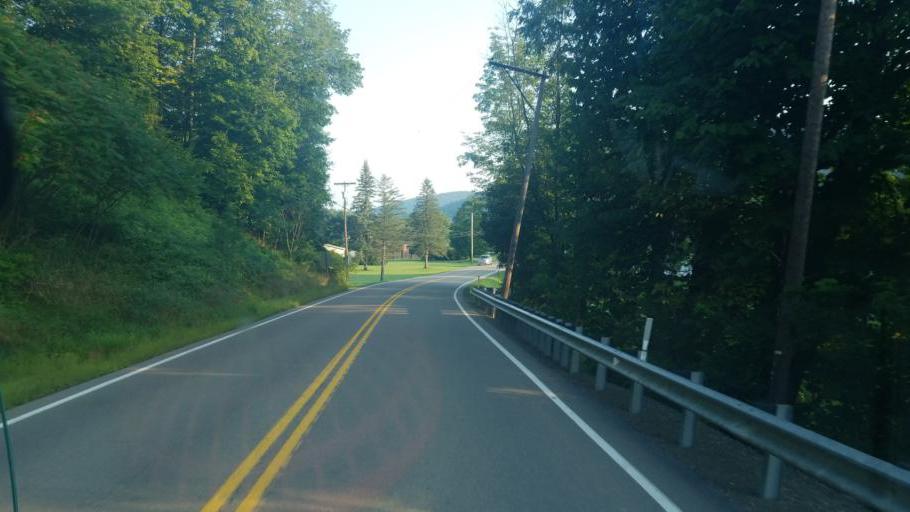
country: US
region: Pennsylvania
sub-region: Tioga County
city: Westfield
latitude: 41.9589
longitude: -77.4449
